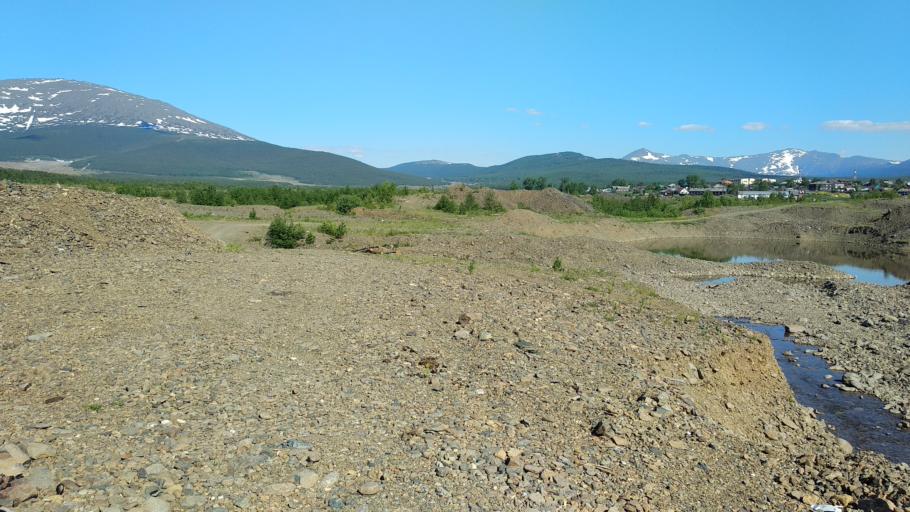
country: RU
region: Sverdlovsk
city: Valerianovsk
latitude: 59.4903
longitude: 59.2050
